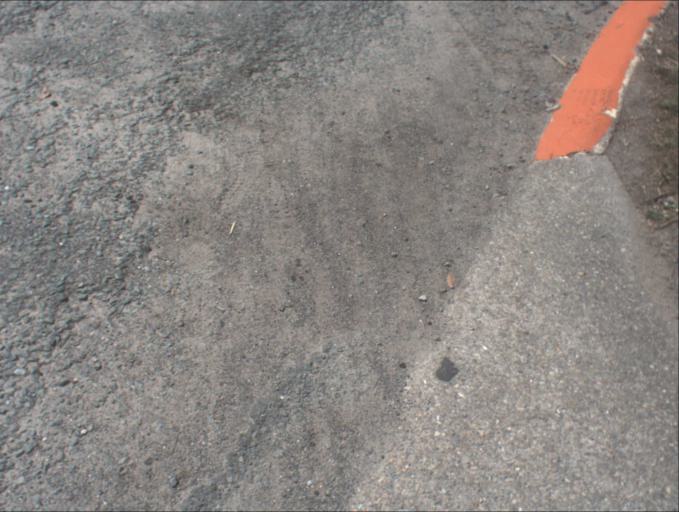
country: AU
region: Queensland
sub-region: Logan
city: Windaroo
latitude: -27.7343
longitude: 153.1934
